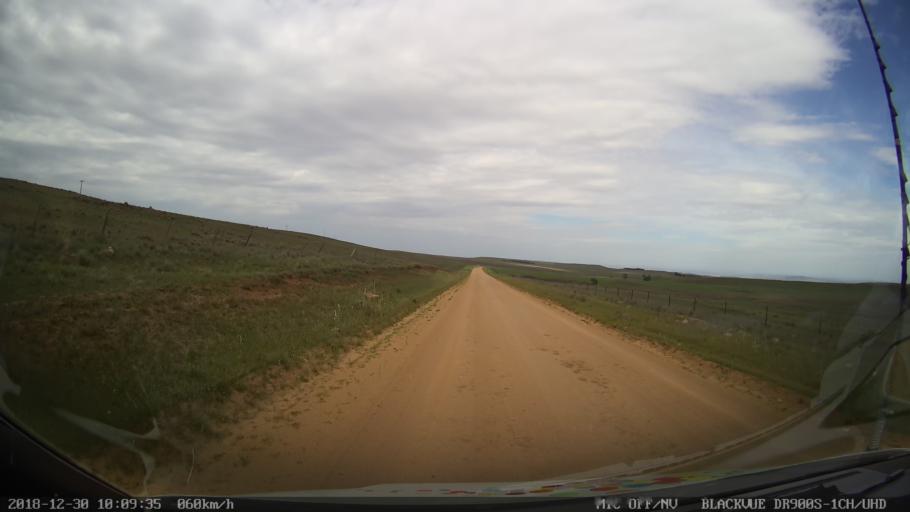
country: AU
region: New South Wales
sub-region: Cooma-Monaro
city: Cooma
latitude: -36.5488
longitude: 149.1040
